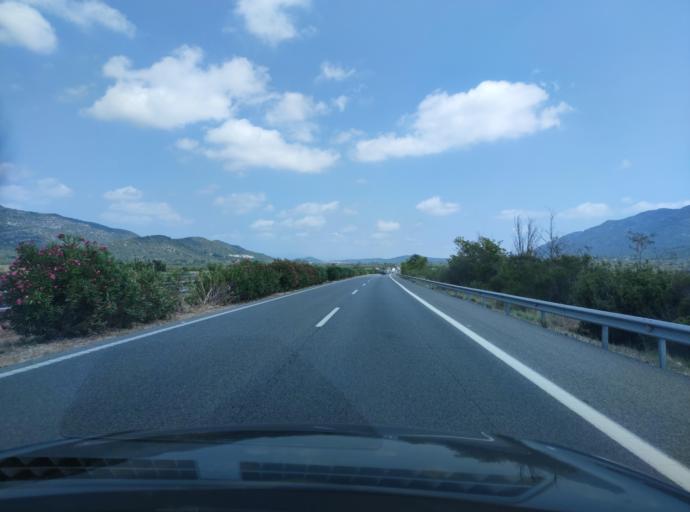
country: ES
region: Catalonia
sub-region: Provincia de Tarragona
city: Ulldecona
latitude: 40.6259
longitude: 0.4903
